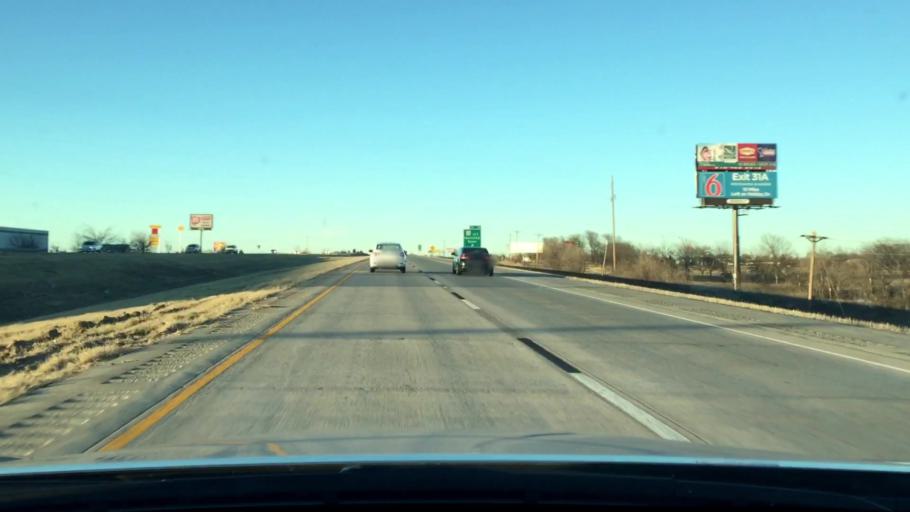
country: US
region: Oklahoma
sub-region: Love County
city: Marietta
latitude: 33.9340
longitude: -97.1347
